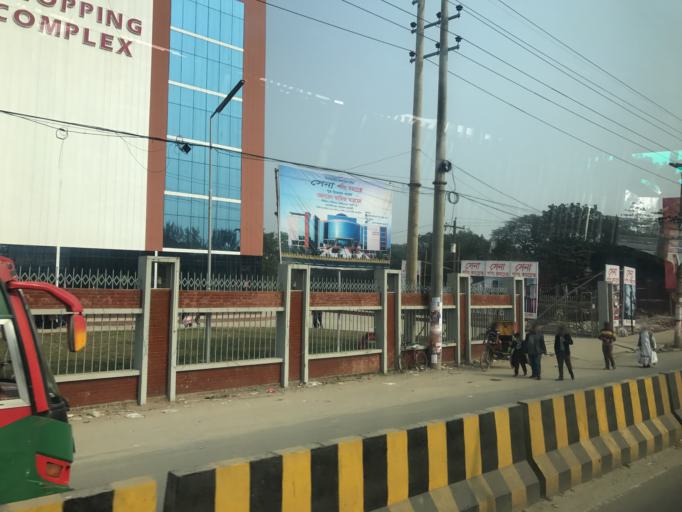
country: BD
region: Dhaka
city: Tungi
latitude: 23.9123
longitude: 90.2600
